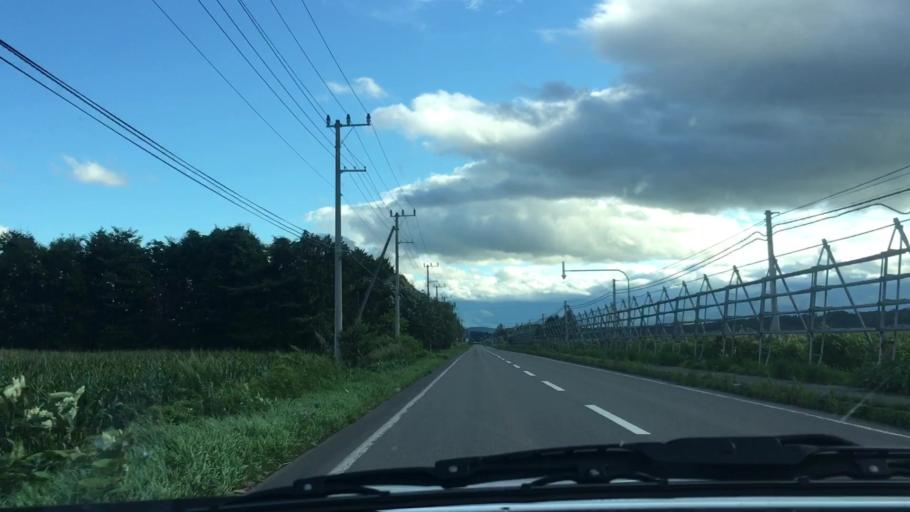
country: JP
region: Hokkaido
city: Otofuke
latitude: 43.1430
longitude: 142.8968
